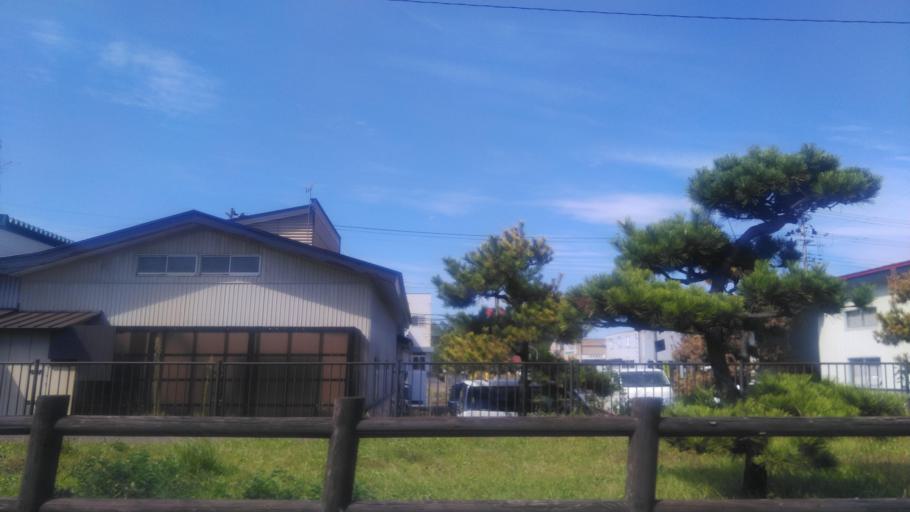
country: JP
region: Akita
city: Noshiromachi
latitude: 40.1877
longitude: 140.0129
